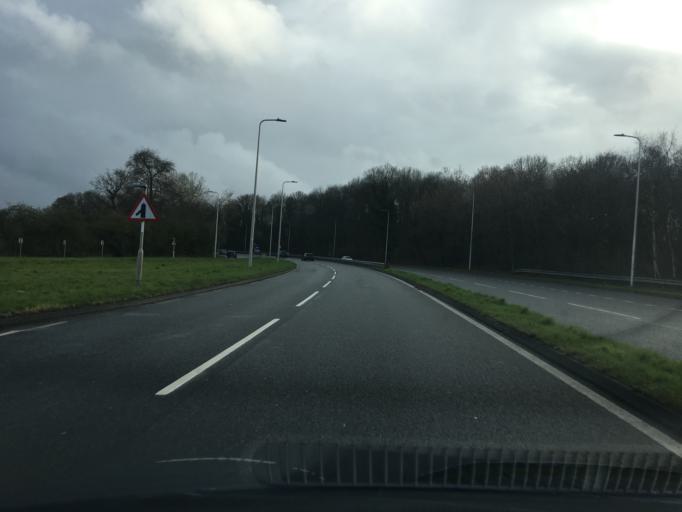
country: GB
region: England
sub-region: Bracknell Forest
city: Bracknell
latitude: 51.4073
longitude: -0.7683
